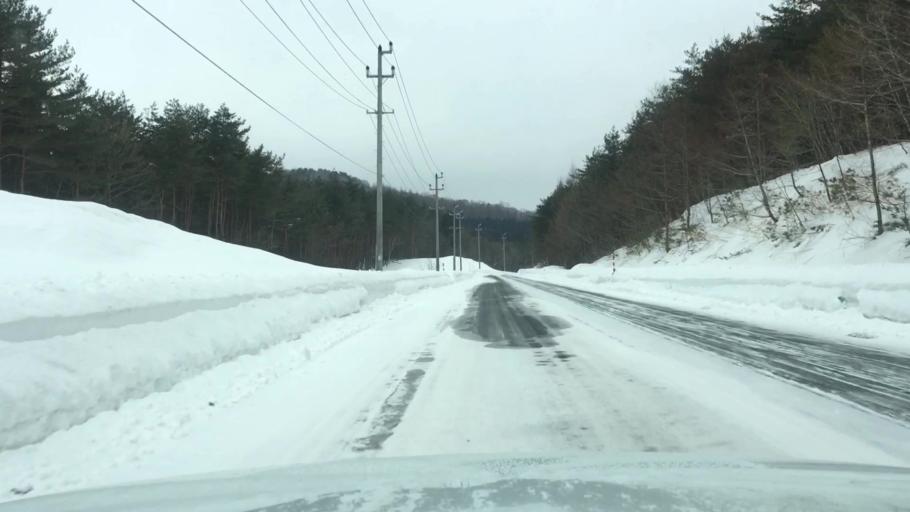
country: JP
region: Iwate
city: Shizukuishi
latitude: 39.9737
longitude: 141.0023
